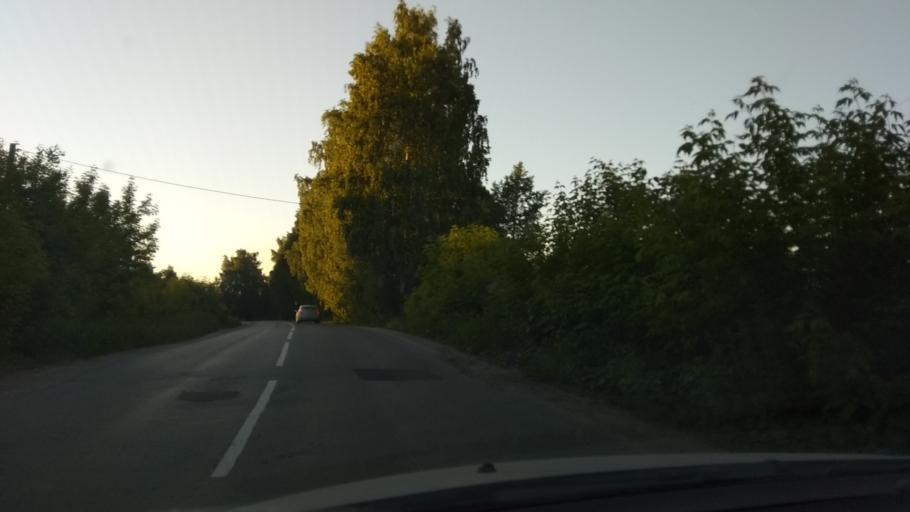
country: RU
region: Sverdlovsk
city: Sredneuralsk
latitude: 56.9796
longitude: 60.4609
